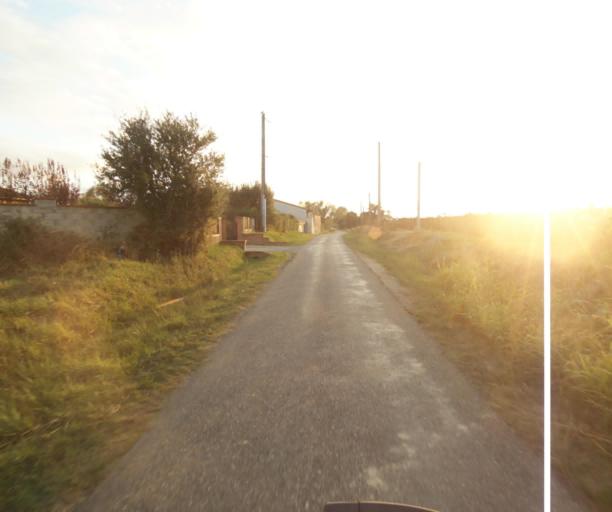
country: FR
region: Midi-Pyrenees
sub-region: Departement du Tarn-et-Garonne
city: Verdun-sur-Garonne
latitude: 43.8206
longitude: 1.2045
